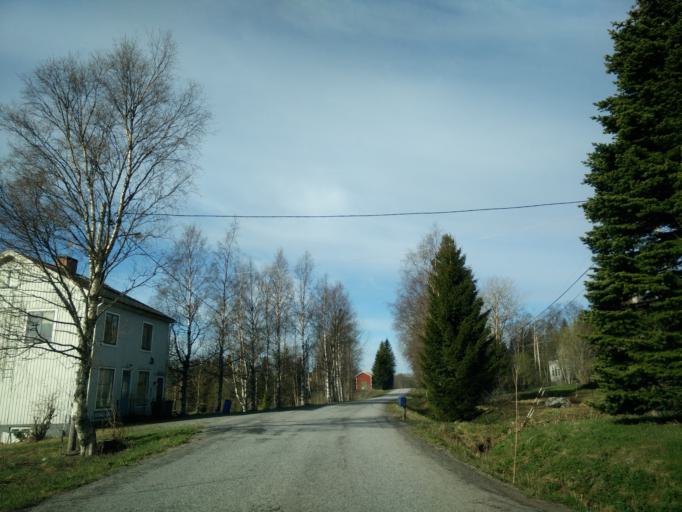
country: SE
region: Vaesternorrland
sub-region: Haernoesands Kommun
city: Haernoesand
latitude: 62.5878
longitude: 17.7834
